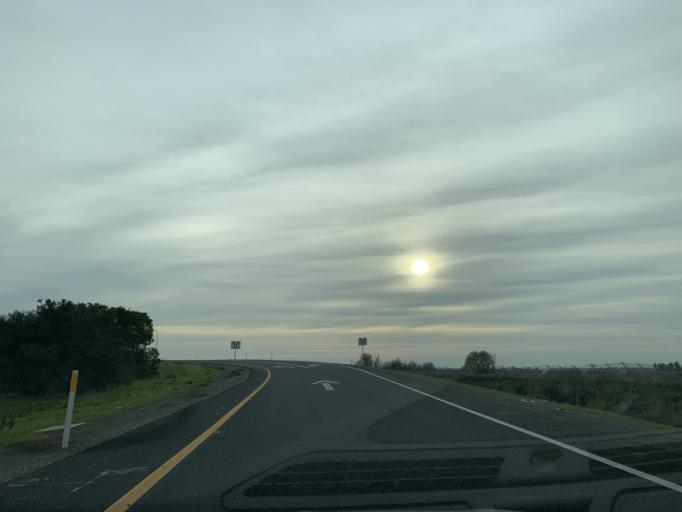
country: US
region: California
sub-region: Sacramento County
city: Elverta
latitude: 38.6872
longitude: -121.5412
